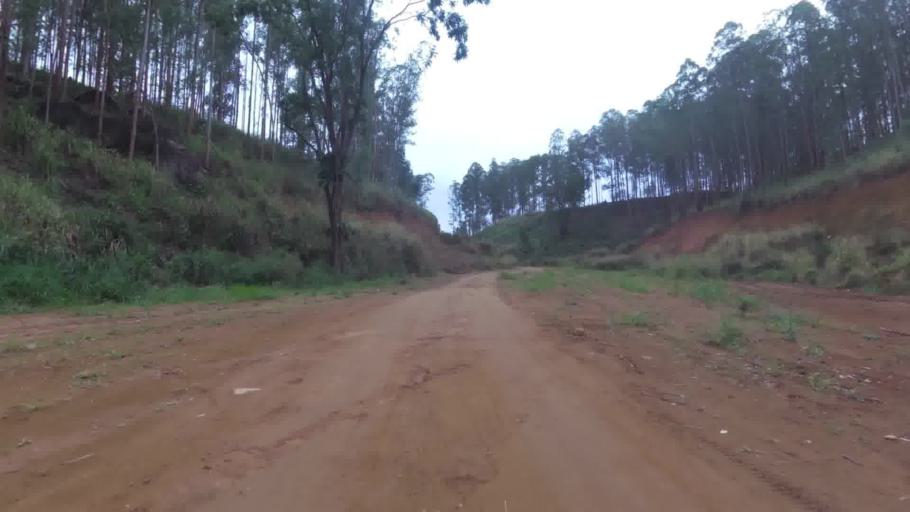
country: BR
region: Espirito Santo
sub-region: Iconha
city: Iconha
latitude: -20.7973
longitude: -40.8142
